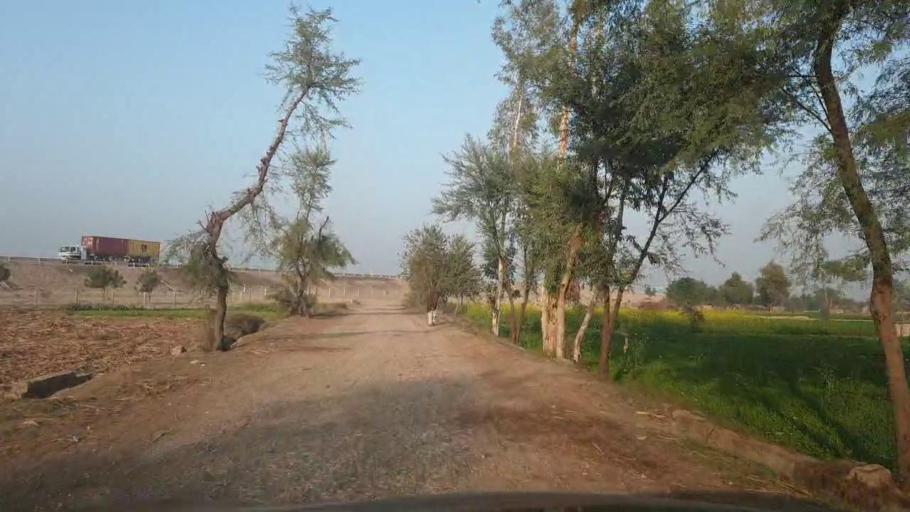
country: PK
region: Sindh
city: Ubauro
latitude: 28.3220
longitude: 69.7750
